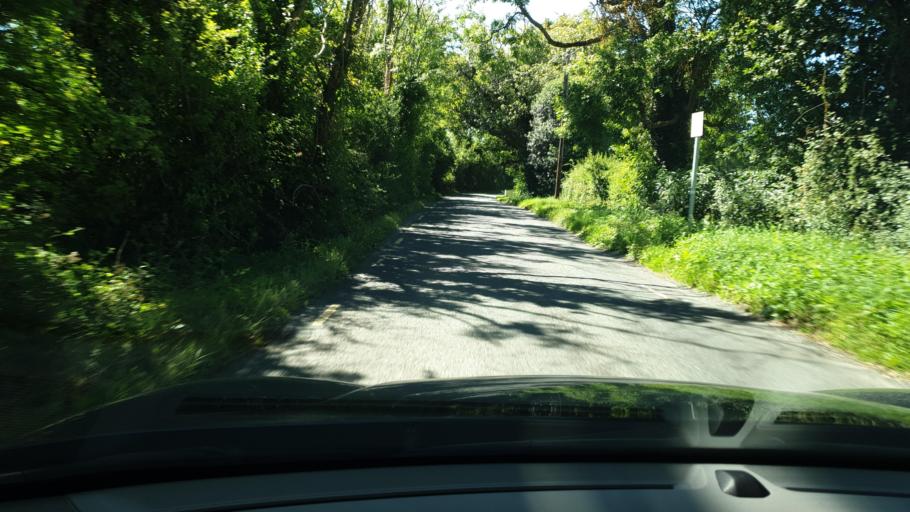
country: IE
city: Confey
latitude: 53.3783
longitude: -6.4776
